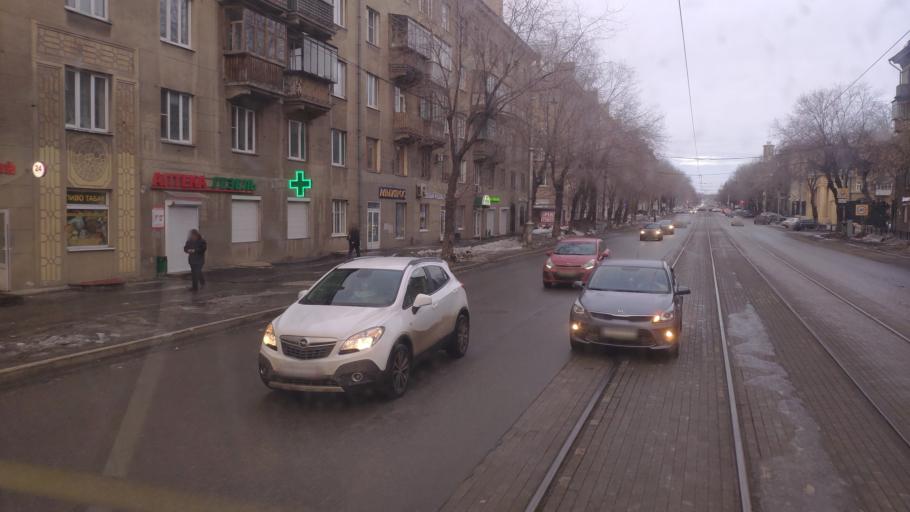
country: RU
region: Chelyabinsk
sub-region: Gorod Magnitogorsk
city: Magnitogorsk
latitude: 53.4178
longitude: 58.9839
